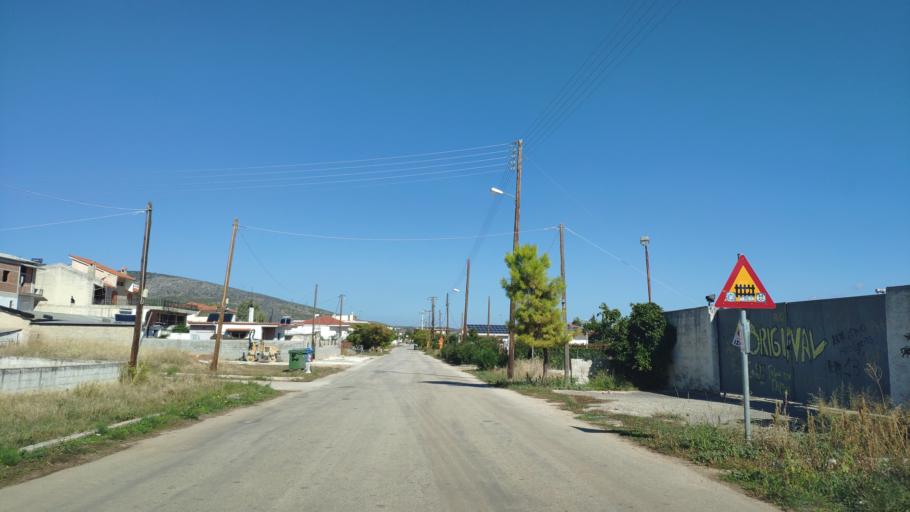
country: GR
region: Peloponnese
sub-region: Nomos Korinthias
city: Khiliomodhi
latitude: 37.8024
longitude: 22.8693
